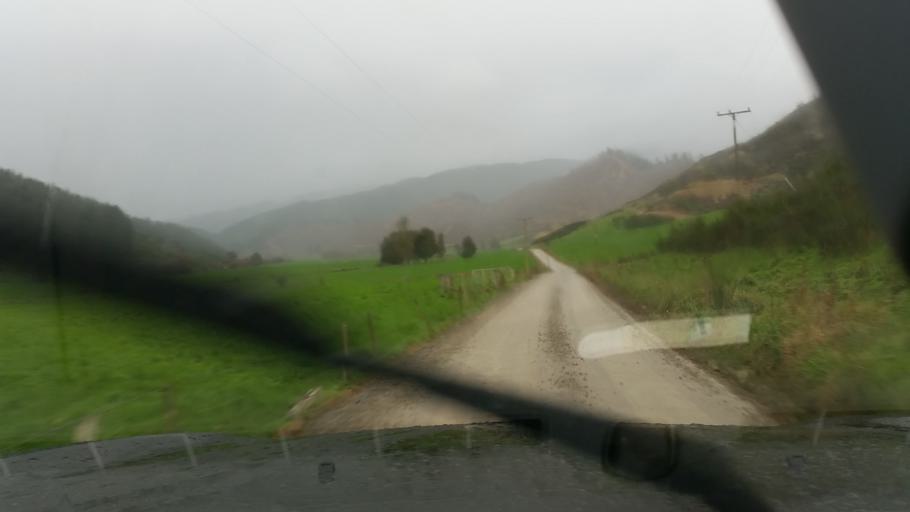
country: NZ
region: Marlborough
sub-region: Marlborough District
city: Picton
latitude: -41.3310
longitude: 173.9345
